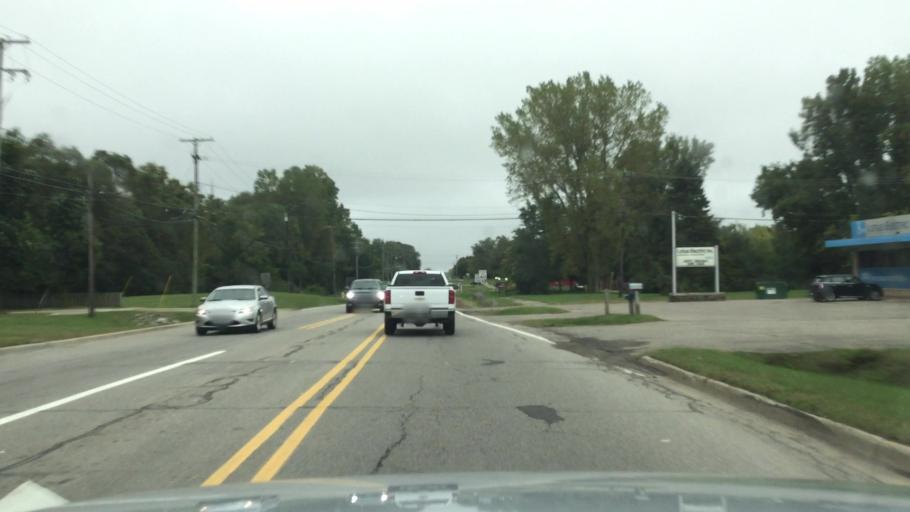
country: US
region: Michigan
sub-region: Oakland County
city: Waterford
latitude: 42.6743
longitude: -83.4067
